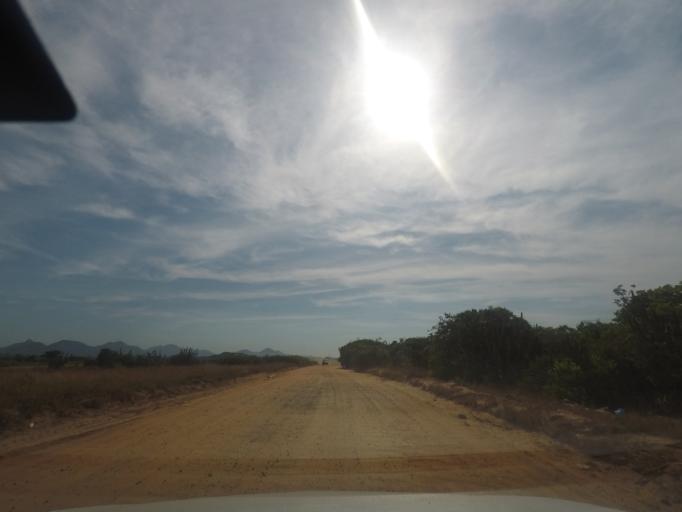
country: BR
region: Rio de Janeiro
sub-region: Marica
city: Marica
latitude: -22.9603
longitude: -42.8480
